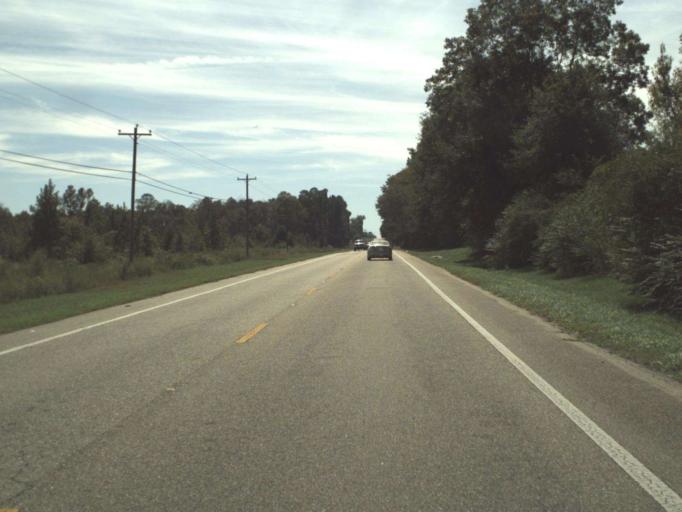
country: US
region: Florida
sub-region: Jackson County
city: Graceville
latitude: 30.9061
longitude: -85.5221
